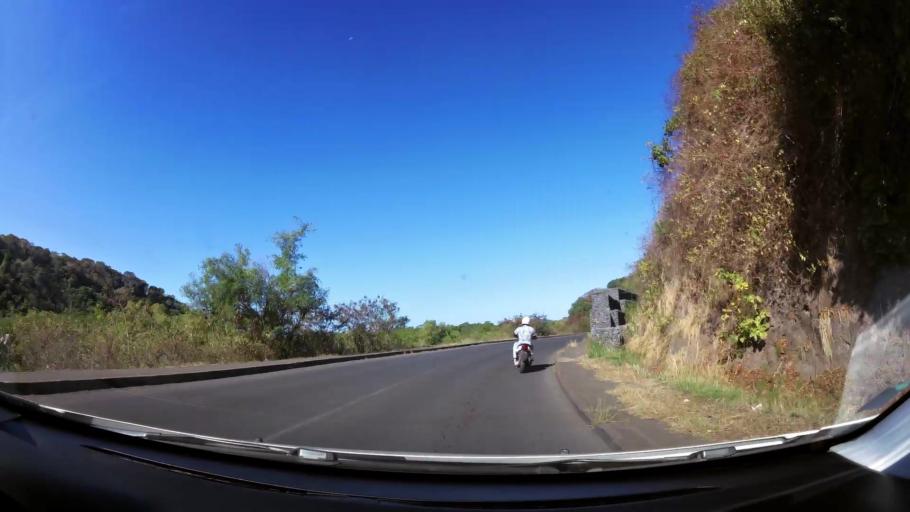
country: YT
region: Mamoudzou
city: Mamoudzou
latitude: -12.7748
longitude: 45.2299
